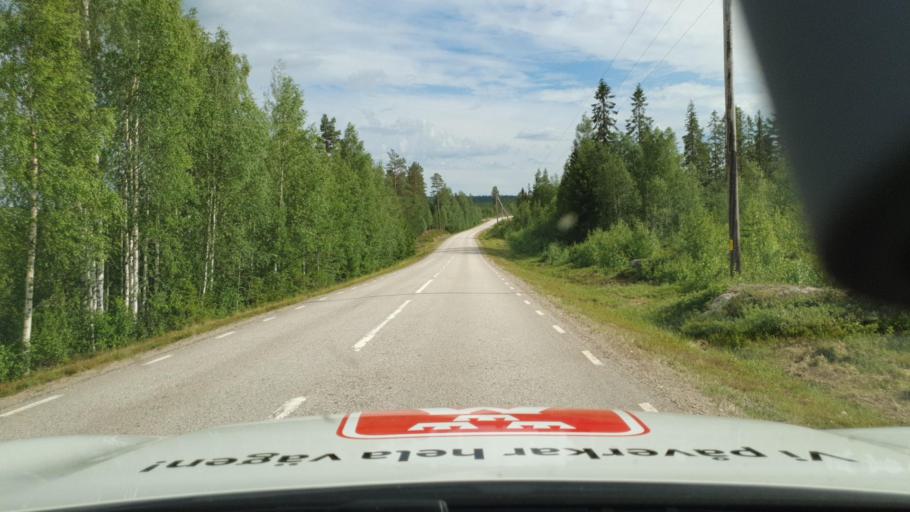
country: NO
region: Hedmark
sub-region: Trysil
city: Innbygda
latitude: 60.9959
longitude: 12.4901
